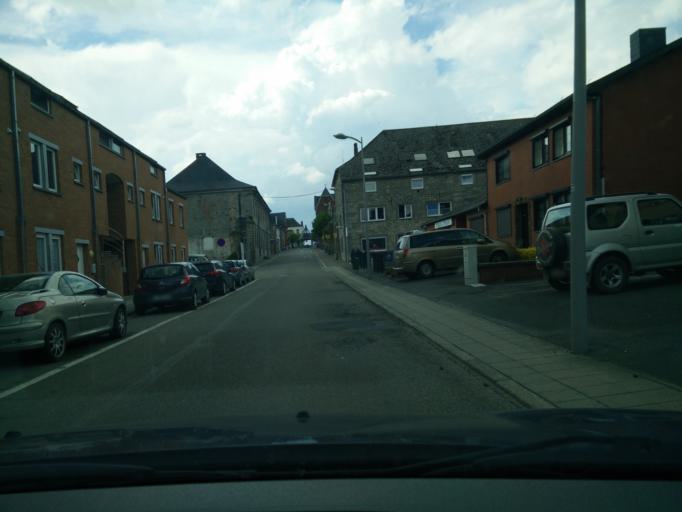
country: BE
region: Wallonia
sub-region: Province de Namur
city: Philippeville
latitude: 50.1945
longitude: 4.5449
